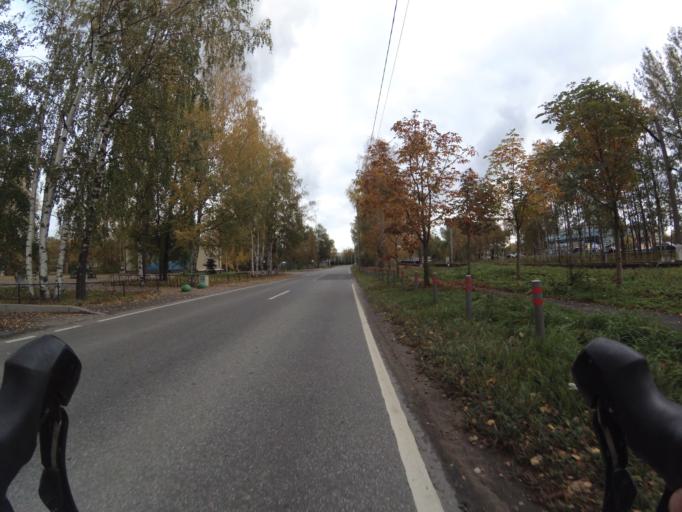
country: RU
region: St.-Petersburg
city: Lakhtinskiy
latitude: 59.9954
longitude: 30.1491
